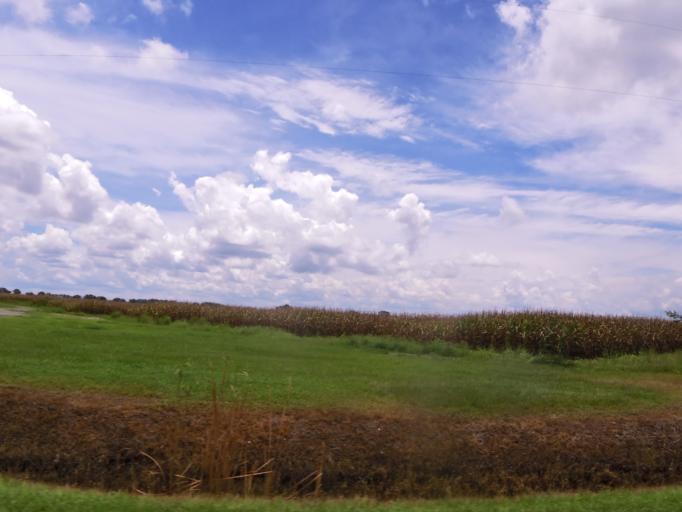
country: US
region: Florida
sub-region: Putnam County
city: East Palatka
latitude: 29.6998
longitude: -81.4973
